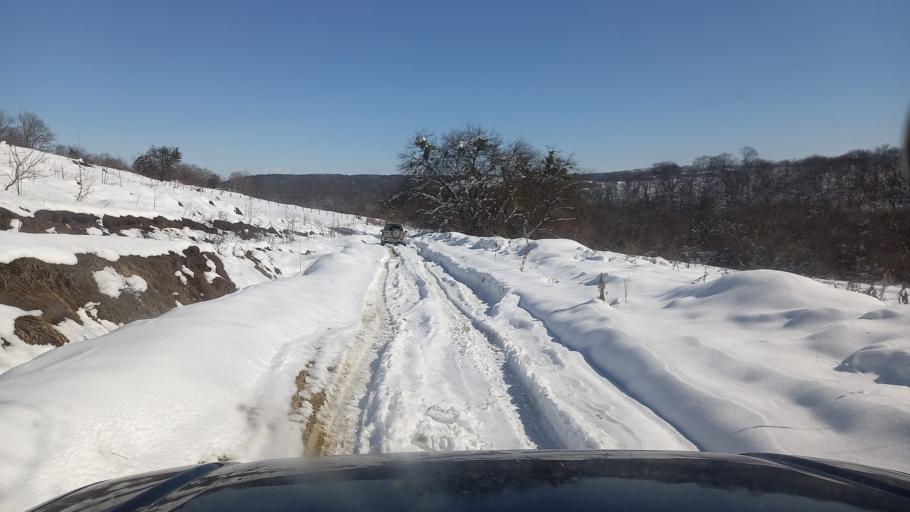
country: RU
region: Krasnodarskiy
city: Gubskaya
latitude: 44.3369
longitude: 40.4475
